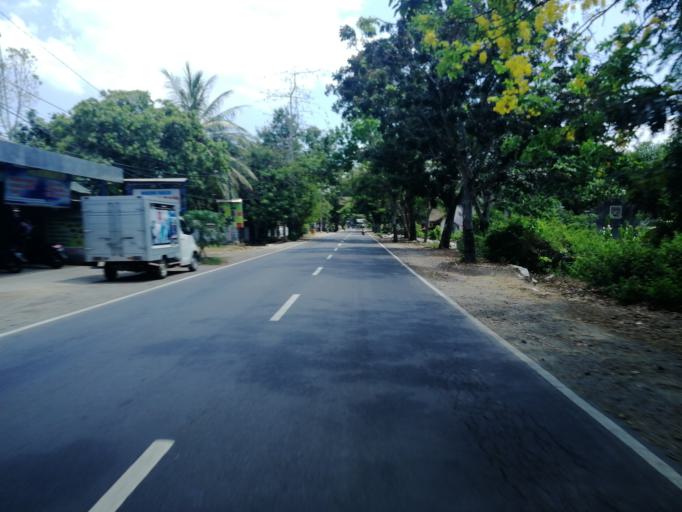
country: ID
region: West Nusa Tenggara
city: Jelateng Timur
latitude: -8.7113
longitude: 116.0766
